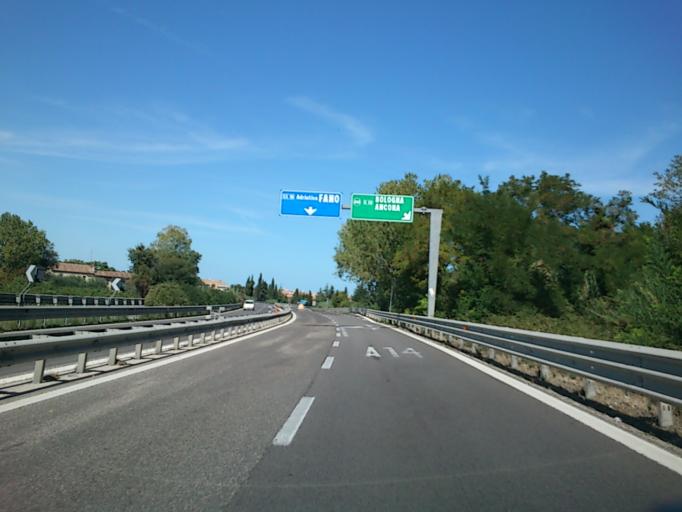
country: IT
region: The Marches
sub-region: Provincia di Pesaro e Urbino
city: Rosciano
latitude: 43.8187
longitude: 13.0166
